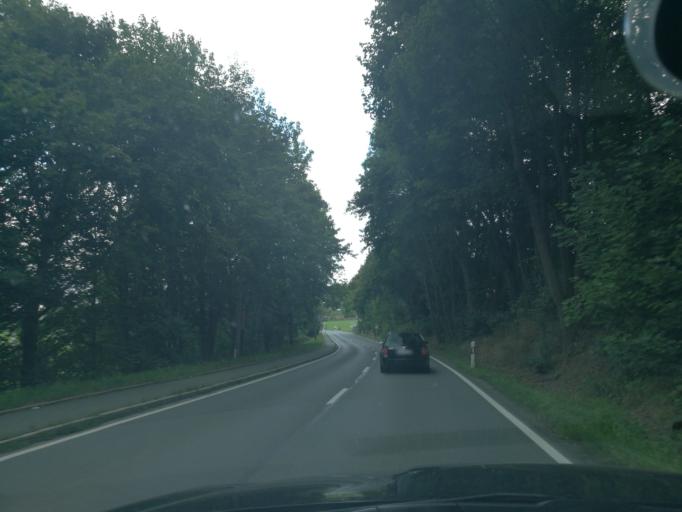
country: DE
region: Saxony
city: Oelsnitz
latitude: 50.4049
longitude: 12.1825
